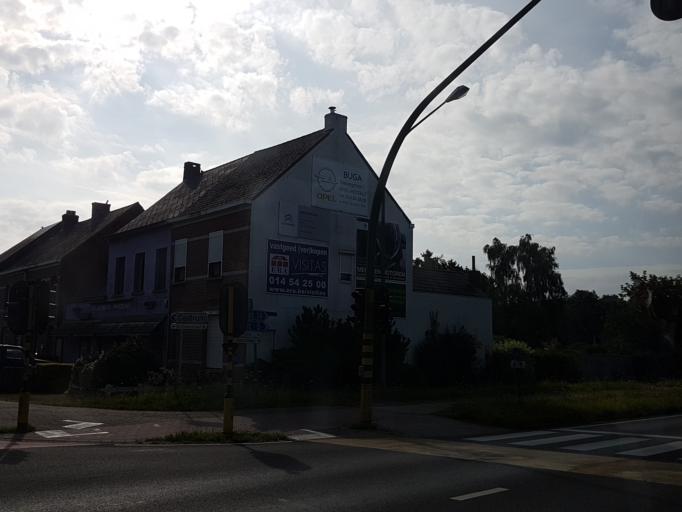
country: BE
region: Flanders
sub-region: Provincie Antwerpen
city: Westerlo
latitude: 51.0857
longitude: 4.9108
